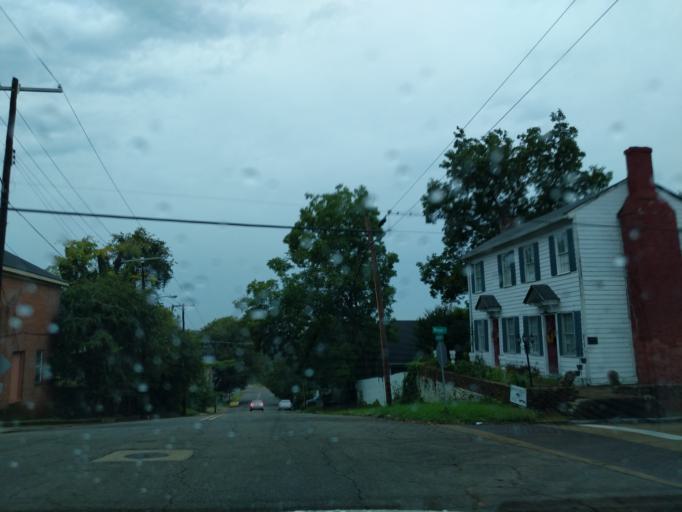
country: US
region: Mississippi
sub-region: Warren County
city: Vicksburg
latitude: 32.3548
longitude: -90.8788
